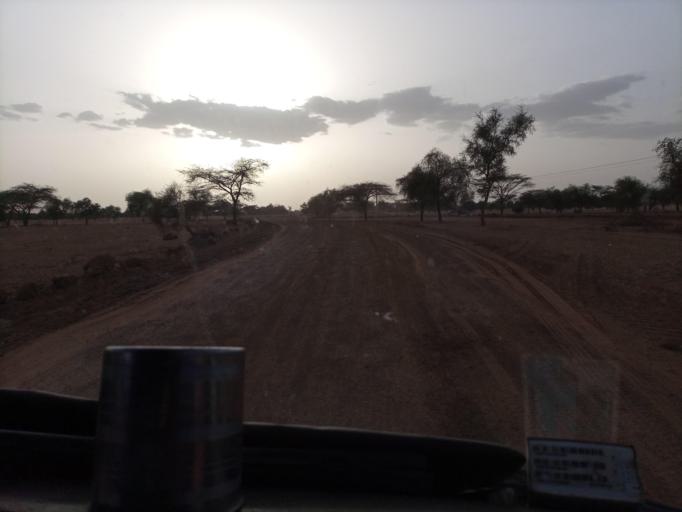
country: SN
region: Louga
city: Dara
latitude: 15.3693
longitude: -15.5754
